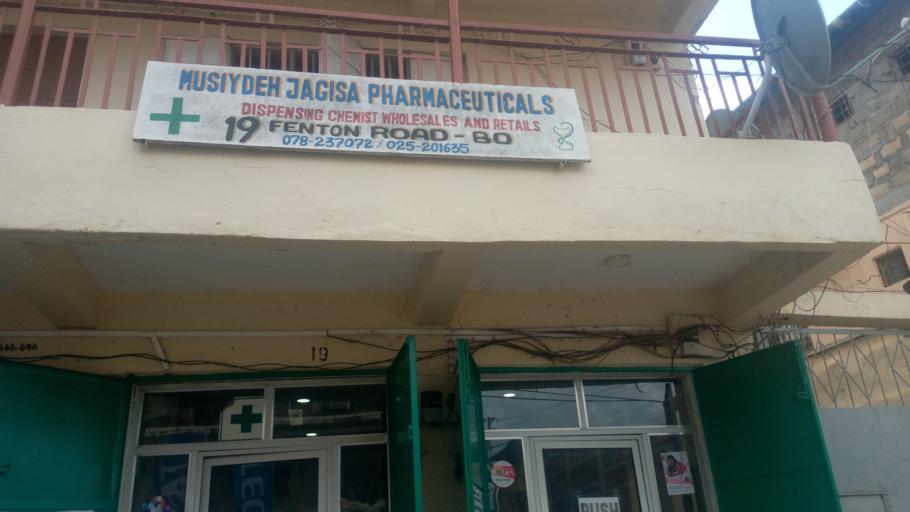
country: SL
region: Southern Province
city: Bo
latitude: 7.9644
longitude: -11.7402
